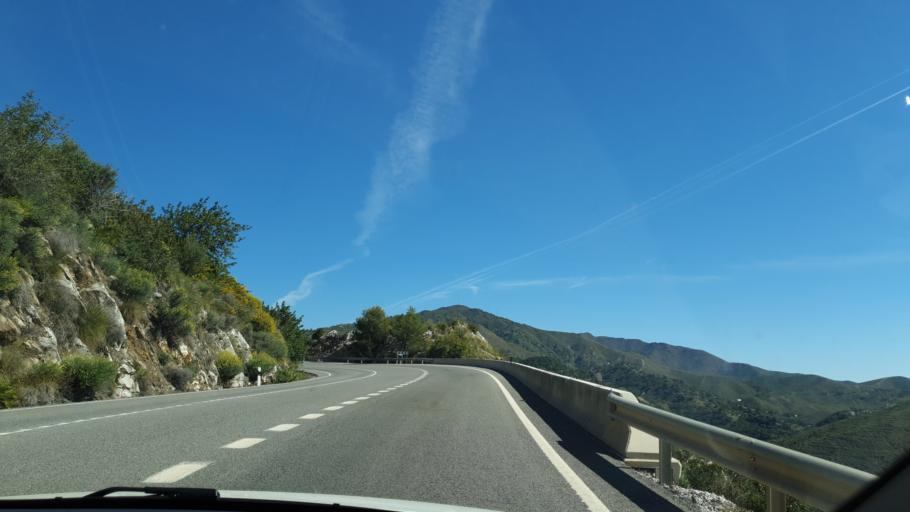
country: ES
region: Andalusia
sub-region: Provincia de Malaga
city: Ojen
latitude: 36.5536
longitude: -4.8627
